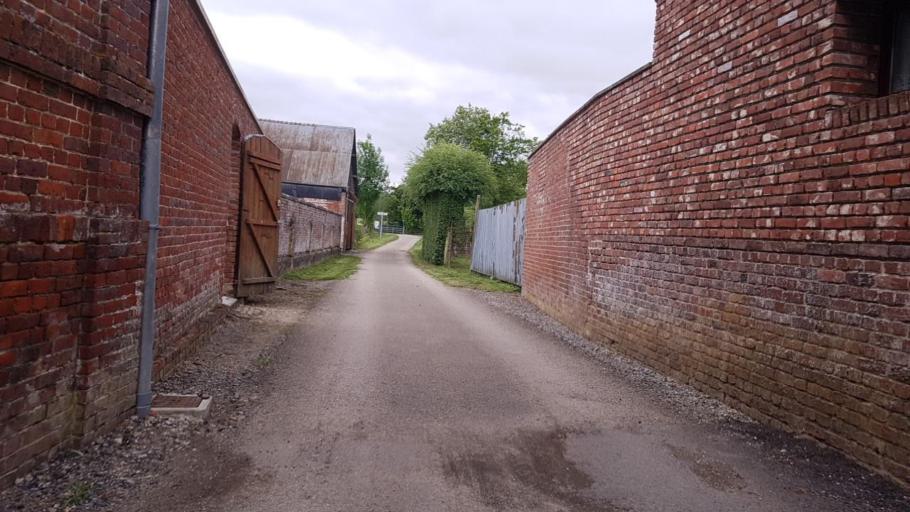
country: FR
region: Picardie
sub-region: Departement de l'Aisne
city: La Capelle
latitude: 49.9073
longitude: 3.8938
